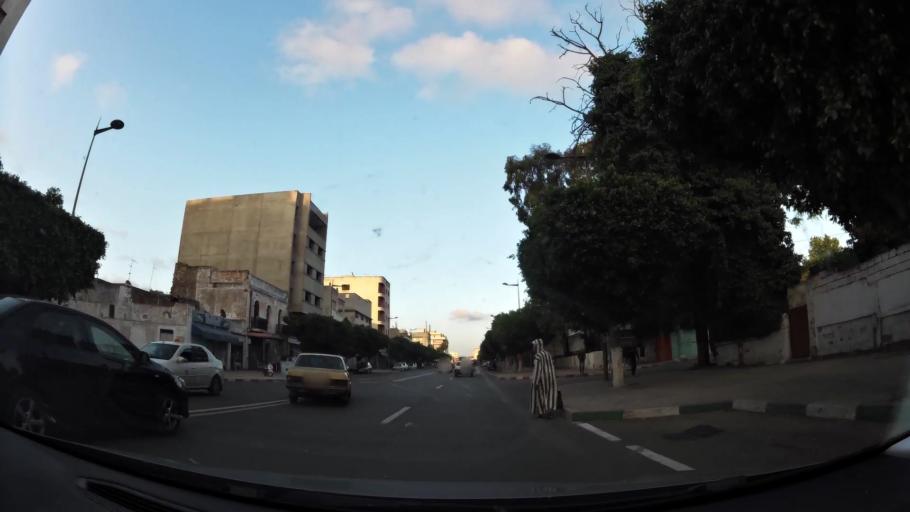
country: MA
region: Gharb-Chrarda-Beni Hssen
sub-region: Kenitra Province
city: Kenitra
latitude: 34.2629
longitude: -6.5740
